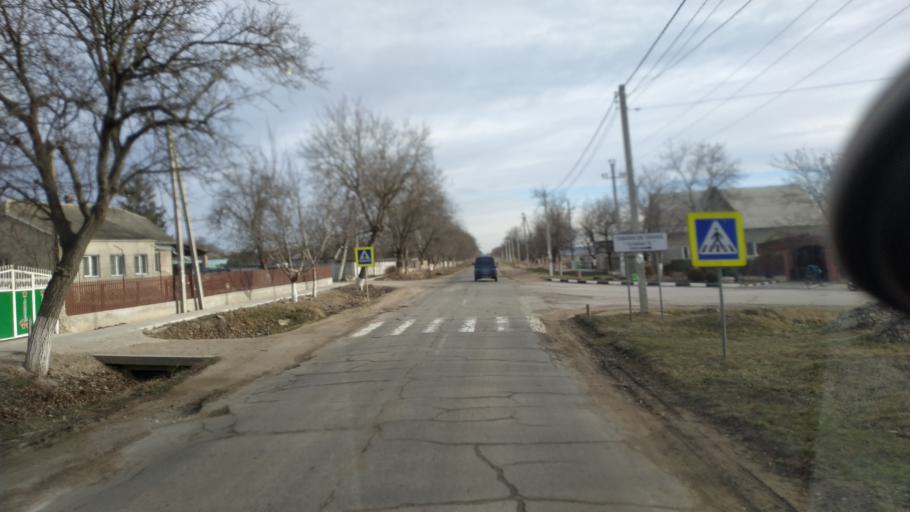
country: MD
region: Criuleni
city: Criuleni
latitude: 47.1687
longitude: 29.1252
